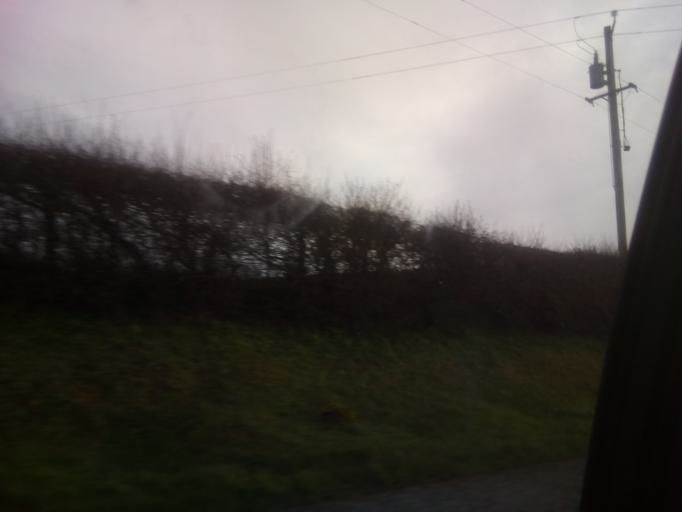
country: IE
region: Leinster
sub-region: Laois
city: Abbeyleix
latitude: 52.8396
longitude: -7.4130
